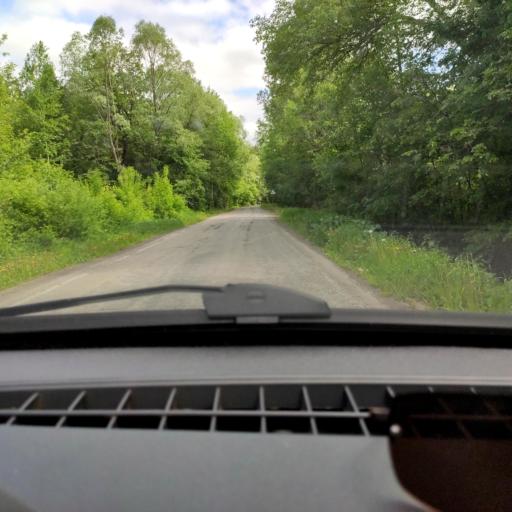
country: RU
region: Bashkortostan
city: Avdon
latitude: 54.6714
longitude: 55.8385
